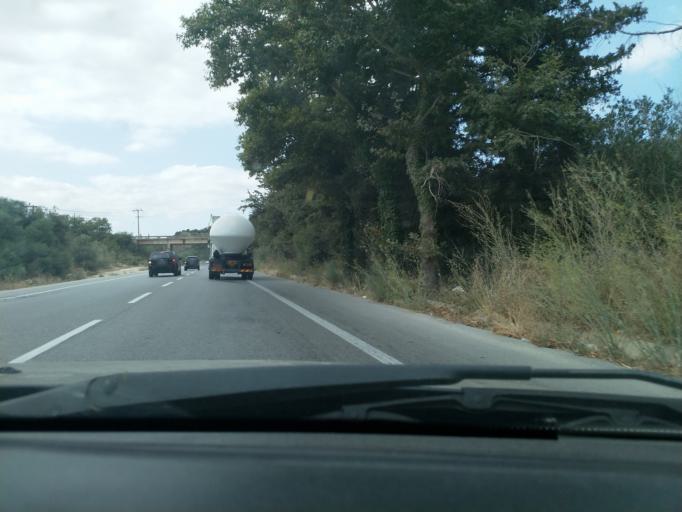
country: GR
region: Crete
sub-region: Nomos Chanias
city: Georgioupolis
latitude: 35.3753
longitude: 24.2089
